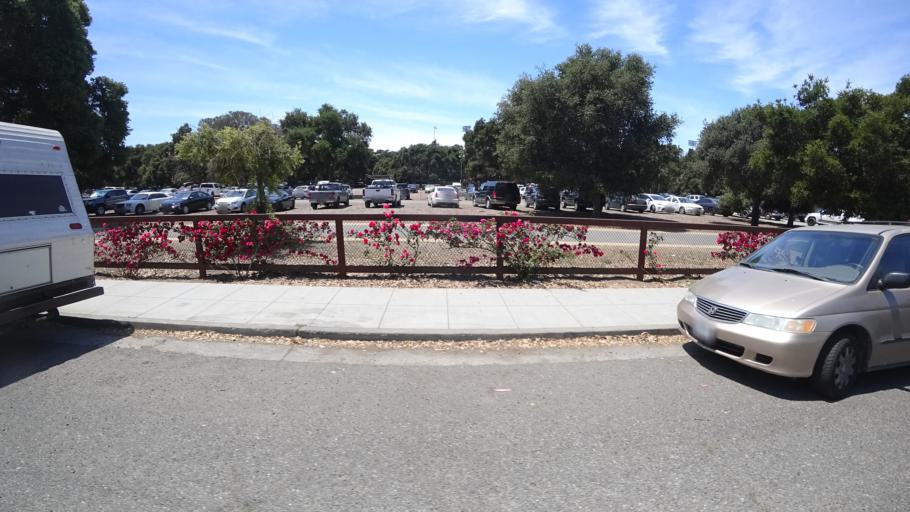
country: US
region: California
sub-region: Santa Clara County
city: Stanford
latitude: 37.4354
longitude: -122.1582
